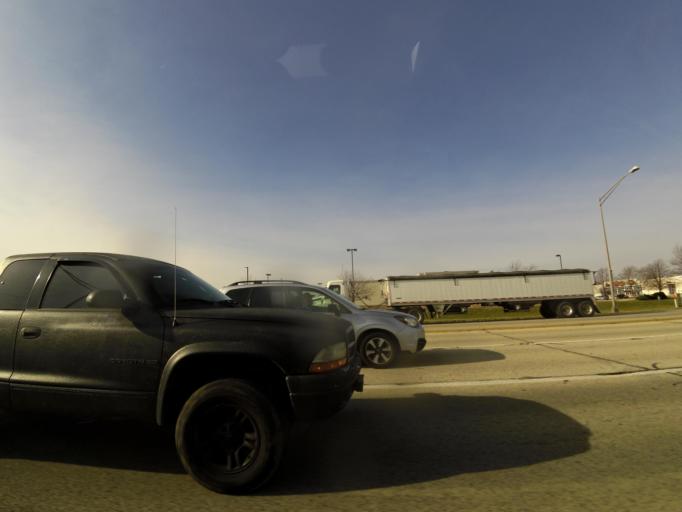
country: US
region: Illinois
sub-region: Macon County
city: Forsyth
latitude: 39.9210
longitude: -88.9554
